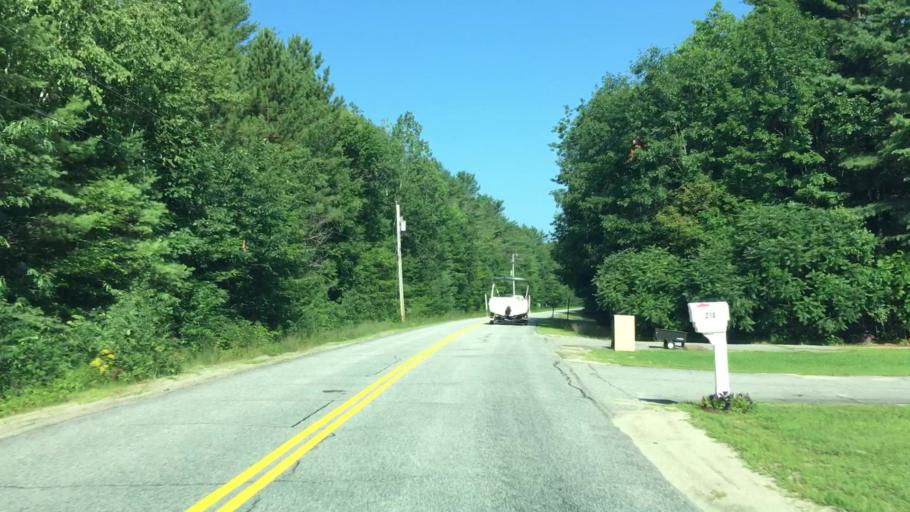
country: US
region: Maine
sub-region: Androscoggin County
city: Poland
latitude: 44.0436
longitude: -70.3554
